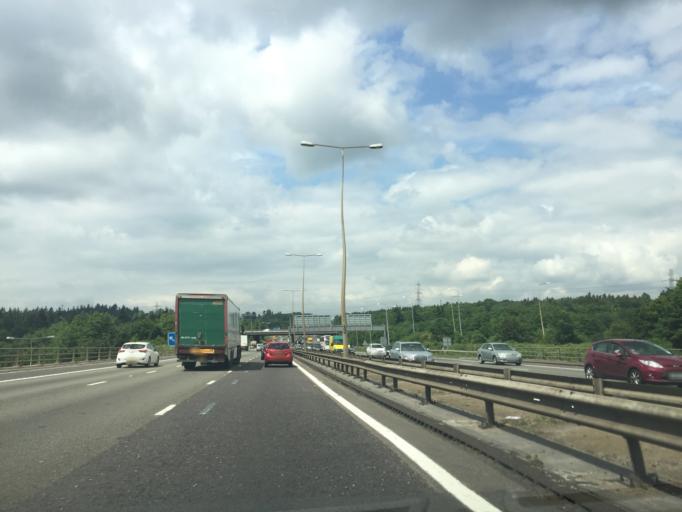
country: GB
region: England
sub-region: Buckinghamshire
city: Denham
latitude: 51.5573
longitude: -0.5294
